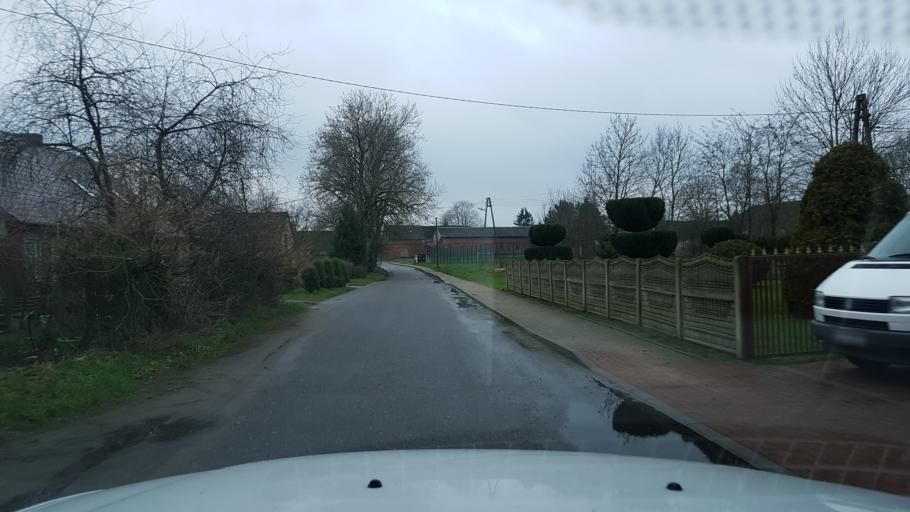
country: PL
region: West Pomeranian Voivodeship
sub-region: Powiat gryficki
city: Brojce
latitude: 53.9684
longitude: 15.3007
